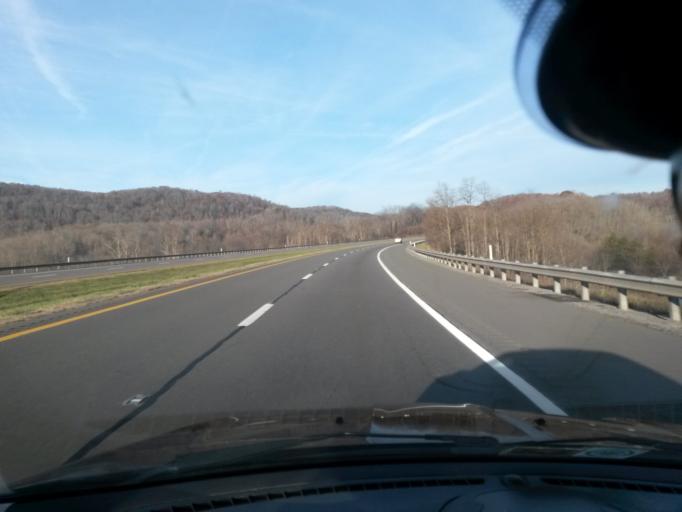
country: US
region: West Virginia
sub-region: Greenbrier County
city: Lewisburg
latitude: 37.8521
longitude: -80.5040
